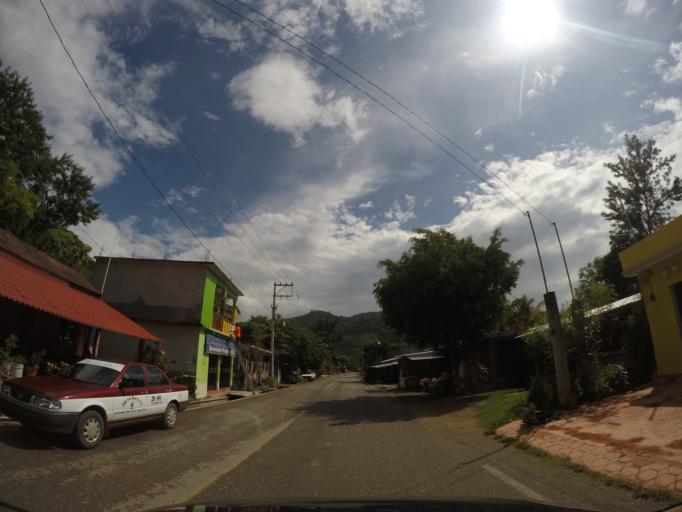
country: MX
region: Oaxaca
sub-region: San Jeronimo Coatlan
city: San Cristobal Honduras
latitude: 16.3564
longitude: -97.0944
